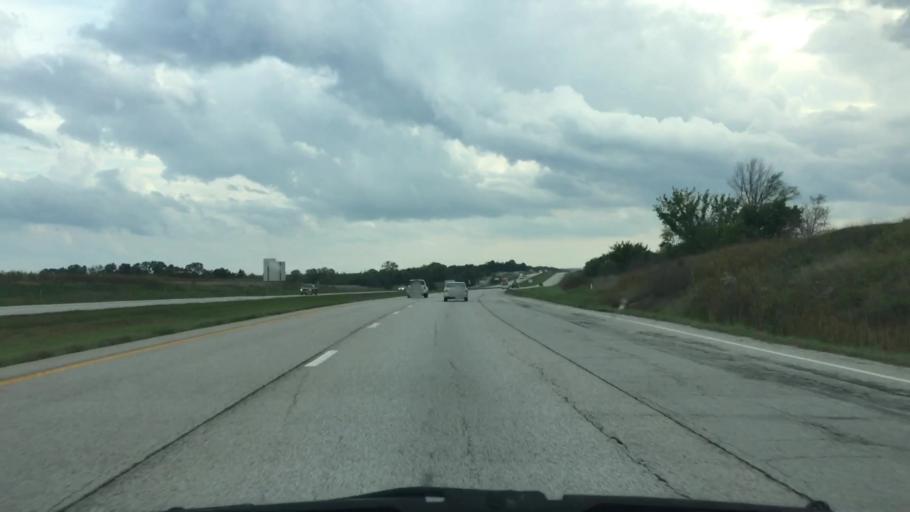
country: US
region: Missouri
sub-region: Clinton County
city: Cameron
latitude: 39.7288
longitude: -94.2208
